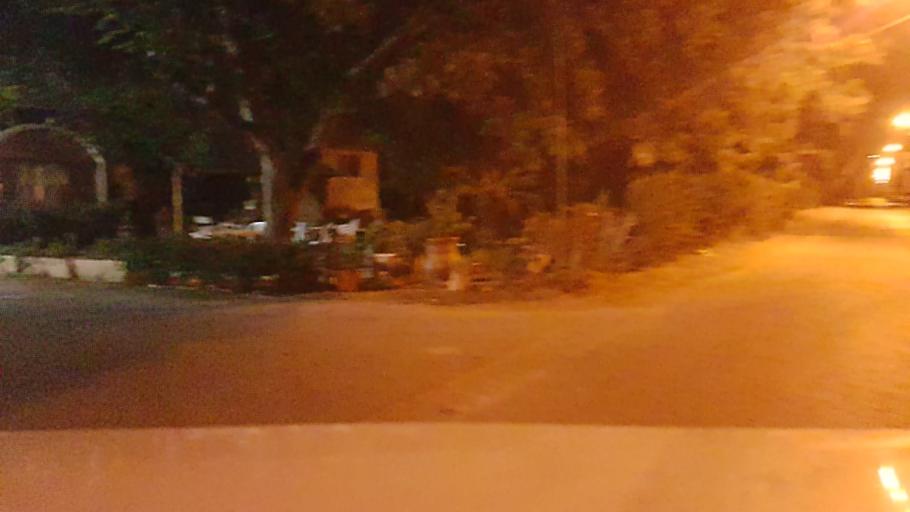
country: IL
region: Central District
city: Nehalim
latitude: 32.0797
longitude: 34.9270
